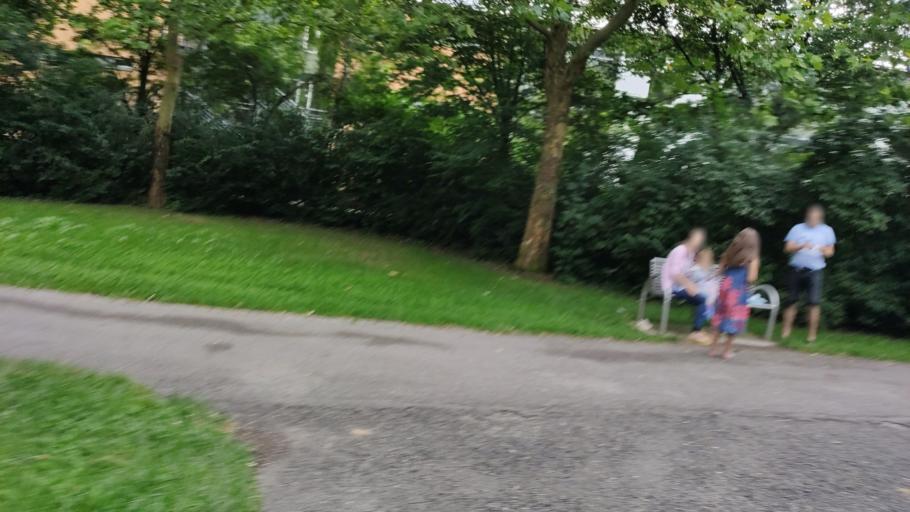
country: DE
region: Bavaria
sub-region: Swabia
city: Konigsbrunn
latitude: 48.2587
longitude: 10.8893
